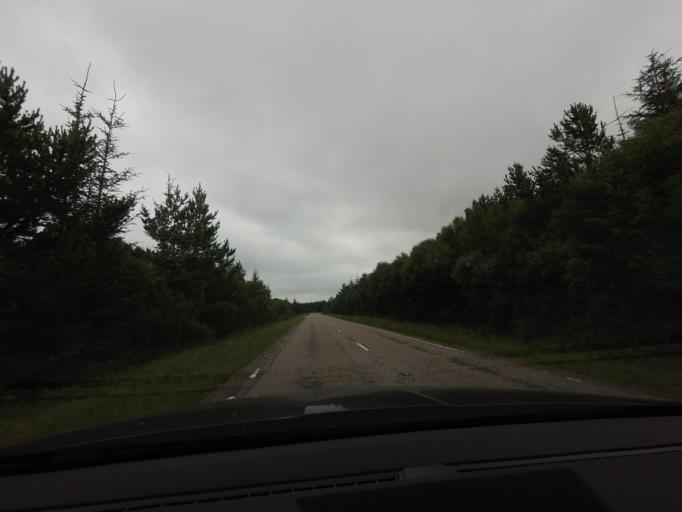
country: GB
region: Scotland
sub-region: Highland
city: Alness
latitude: 57.9951
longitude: -4.4032
